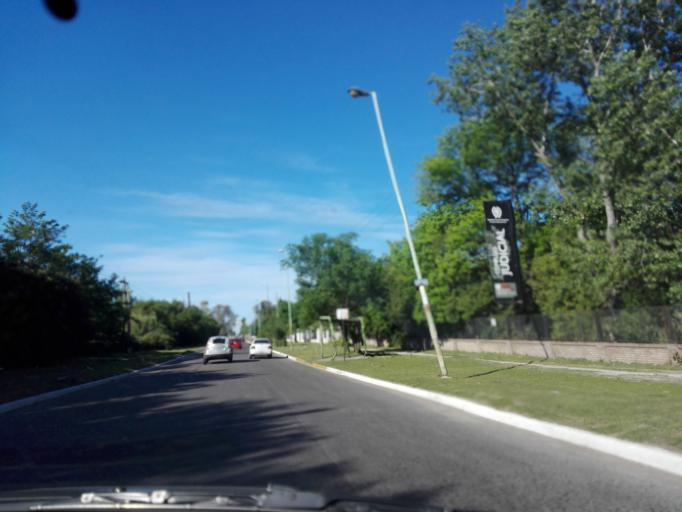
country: AR
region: Buenos Aires
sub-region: Partido de La Plata
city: La Plata
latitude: -34.8966
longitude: -58.0014
